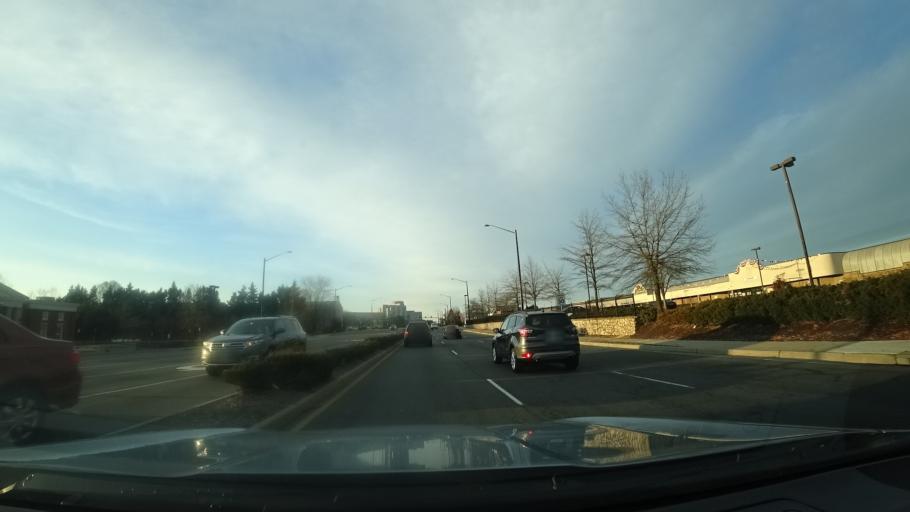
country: US
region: Virginia
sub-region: Fairfax County
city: Herndon
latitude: 38.9628
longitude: -77.3992
